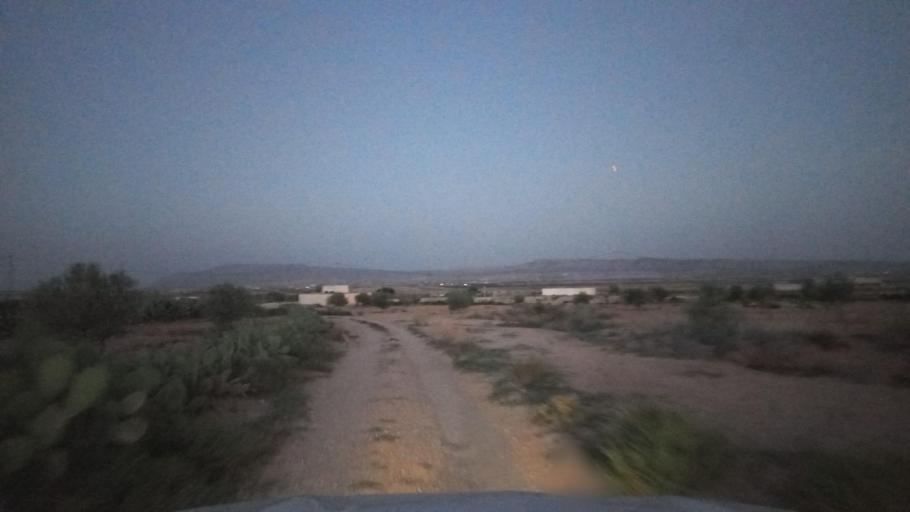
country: TN
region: Al Qasrayn
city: Sbiba
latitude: 35.3789
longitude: 9.0184
